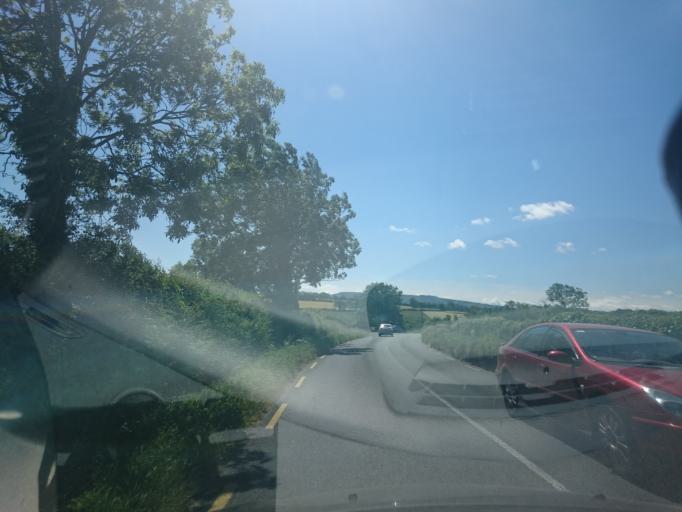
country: IE
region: Leinster
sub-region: County Carlow
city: Bagenalstown
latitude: 52.6279
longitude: -7.0479
